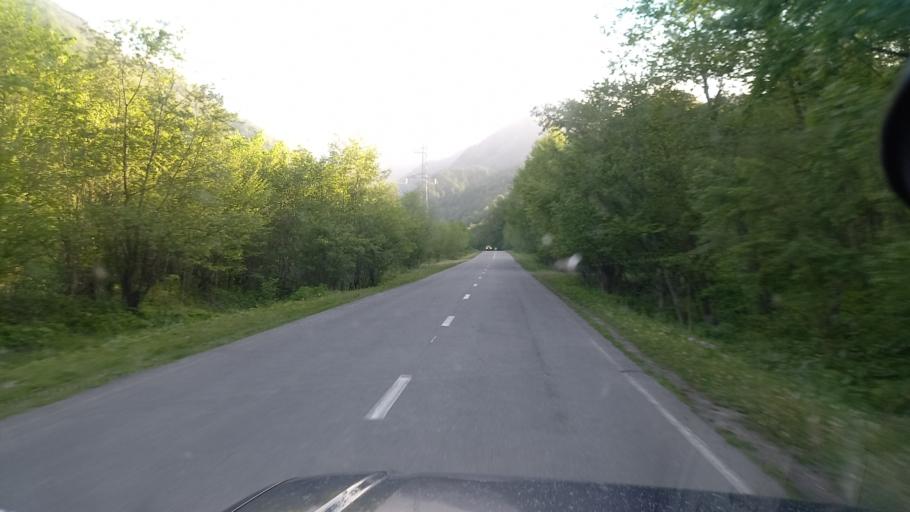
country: RU
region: North Ossetia
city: Tarskoye
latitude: 42.9048
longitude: 44.9563
